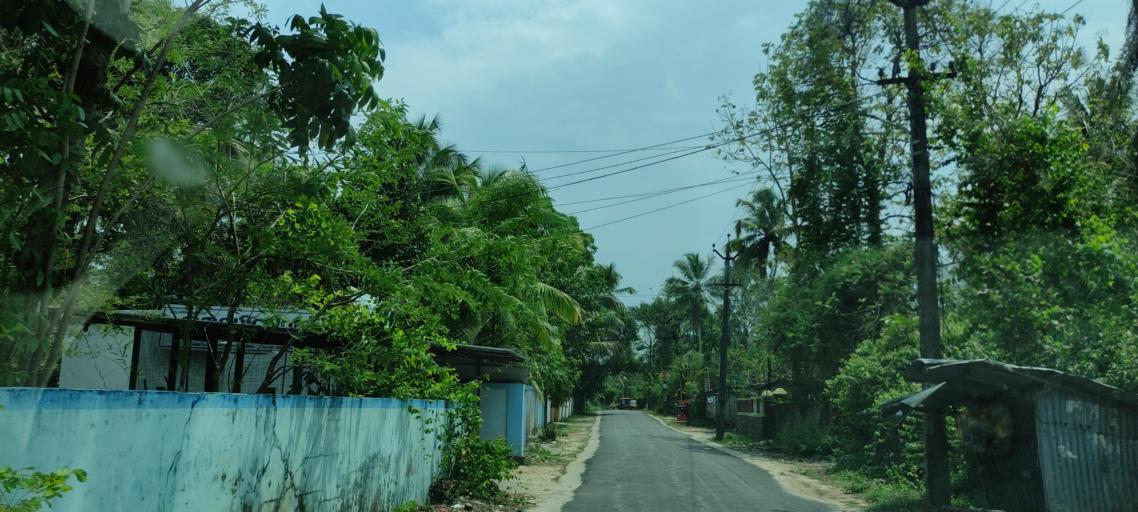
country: IN
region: Kerala
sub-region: Alappuzha
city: Vayalar
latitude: 9.7188
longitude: 76.3407
